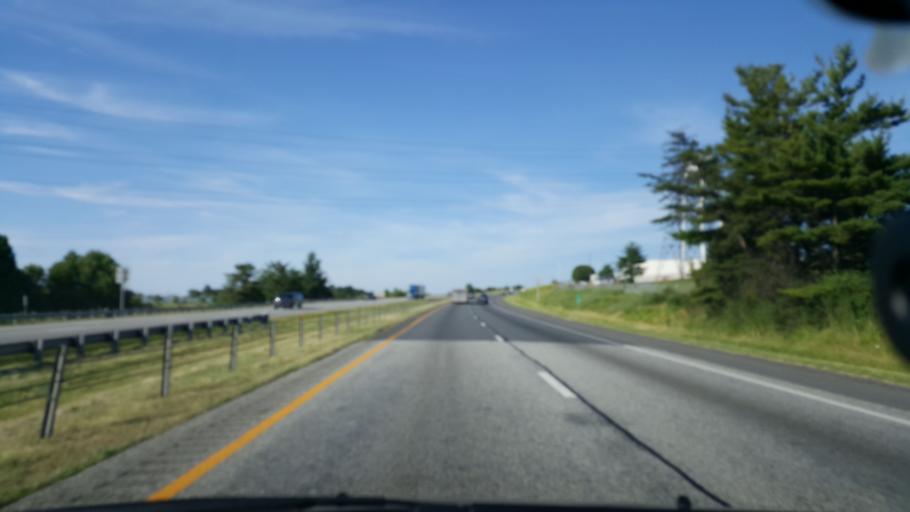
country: US
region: Virginia
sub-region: Rockingham County
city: Dayton
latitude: 38.4045
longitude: -78.9050
